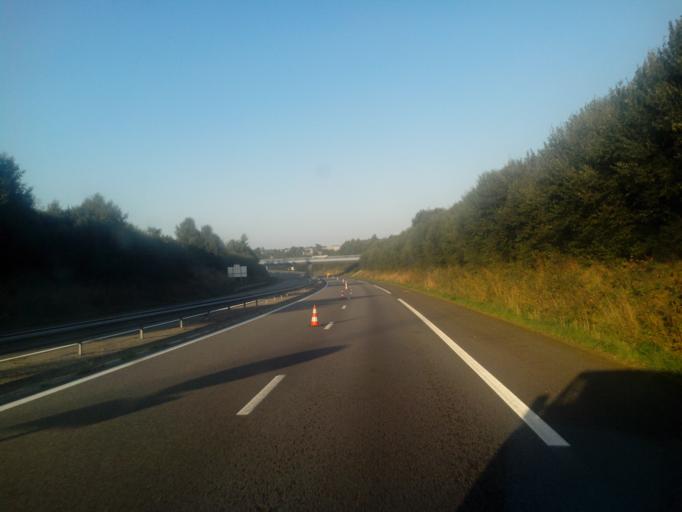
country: FR
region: Brittany
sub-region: Departement du Morbihan
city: Noyal-Pontivy
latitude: 48.1028
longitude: -2.8864
